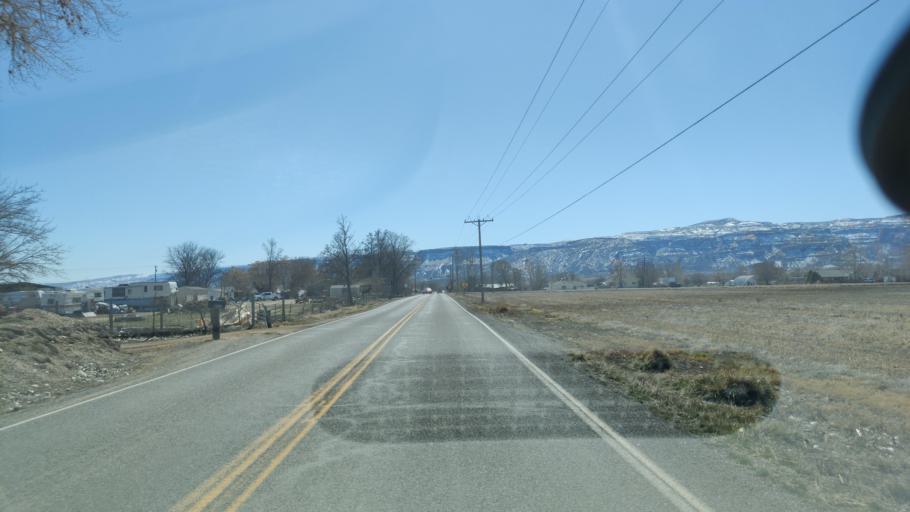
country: US
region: Colorado
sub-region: Mesa County
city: Fruita
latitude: 39.1519
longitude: -108.7011
